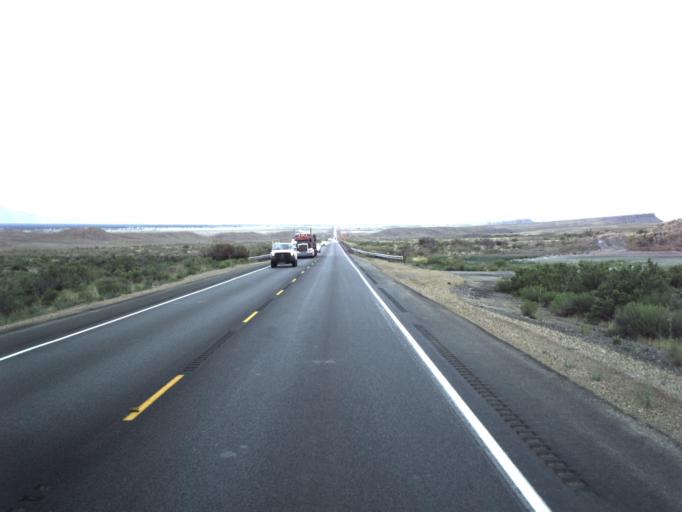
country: US
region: Utah
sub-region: Carbon County
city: East Carbon City
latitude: 39.4685
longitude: -110.4962
